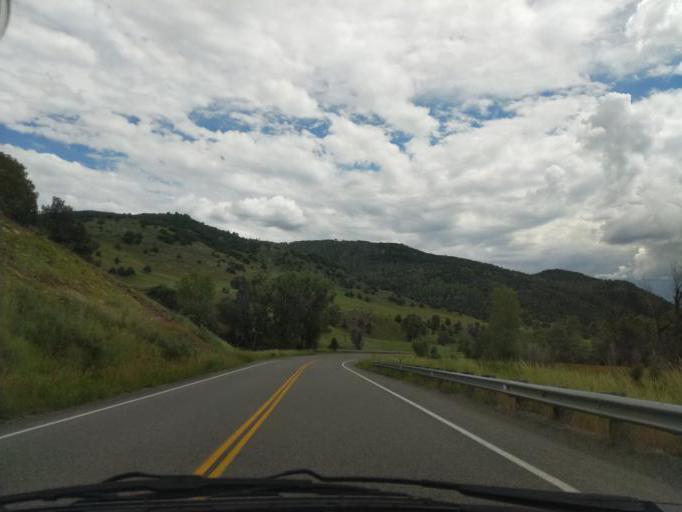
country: US
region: Colorado
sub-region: Delta County
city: Paonia
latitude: 39.0493
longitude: -107.3609
